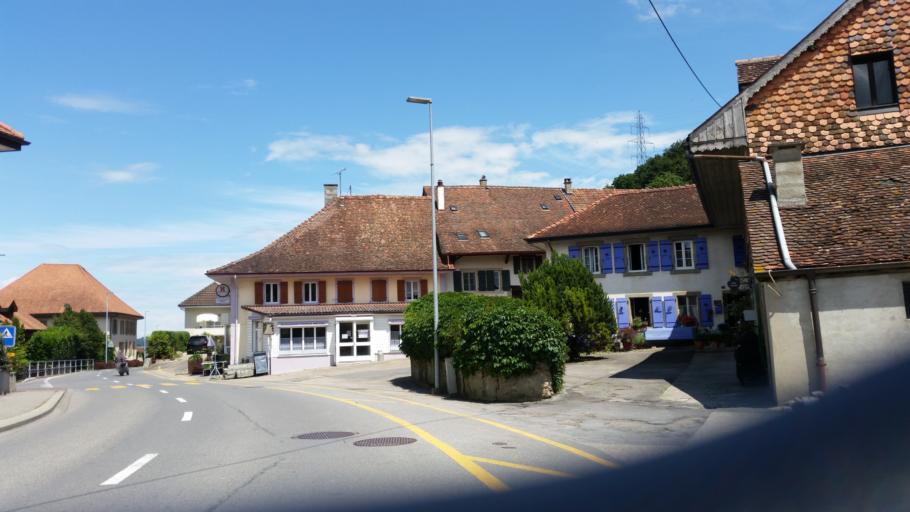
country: CH
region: Vaud
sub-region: Jura-Nord vaudois District
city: Yverdon-les-Bains
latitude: 46.7430
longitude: 6.6090
